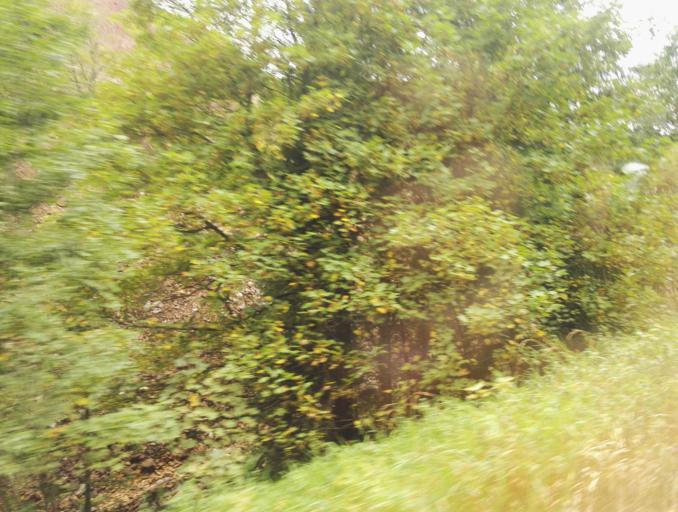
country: AT
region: Styria
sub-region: Politischer Bezirk Leoben
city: Eisenerz
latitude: 47.5270
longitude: 14.9280
